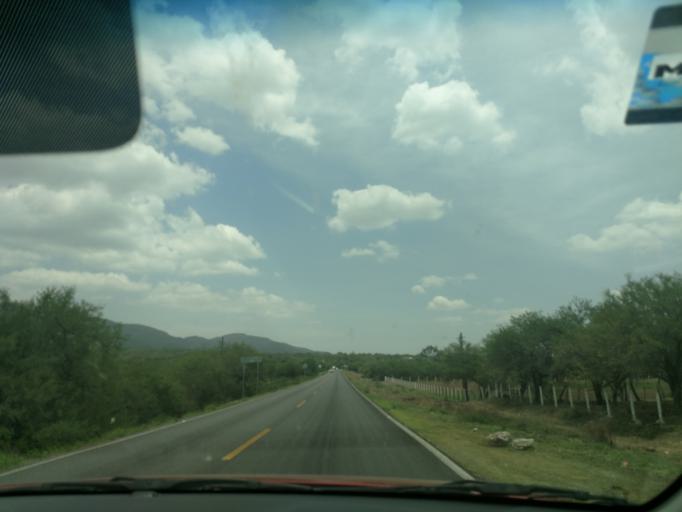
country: MX
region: San Luis Potosi
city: Villa Juarez
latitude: 22.0189
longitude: -100.3844
